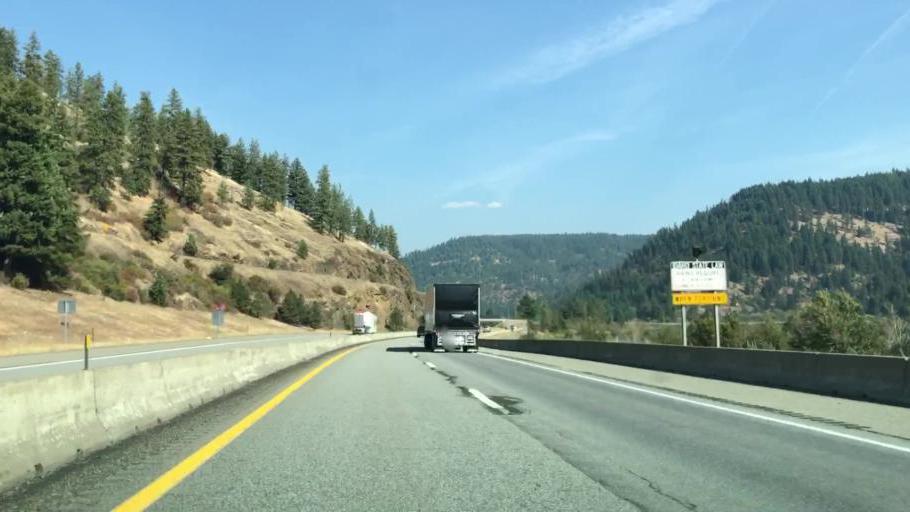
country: US
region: Idaho
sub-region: Kootenai County
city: Coeur d'Alene
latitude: 47.6231
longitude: -116.6588
